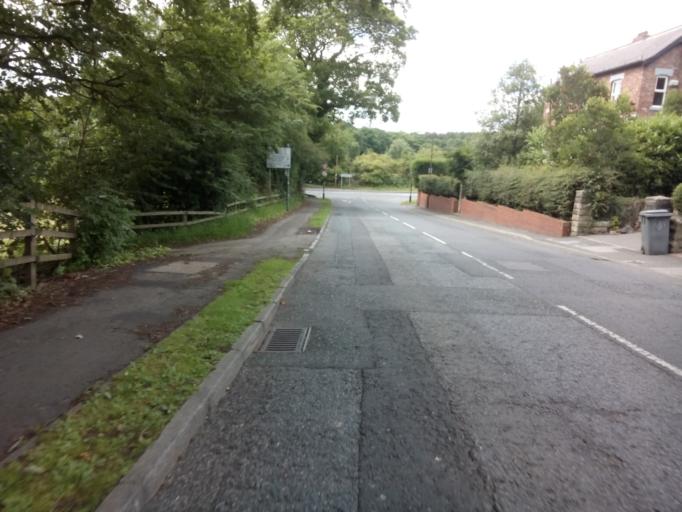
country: GB
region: England
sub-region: County Durham
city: Durham
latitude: 54.7672
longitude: -1.5984
